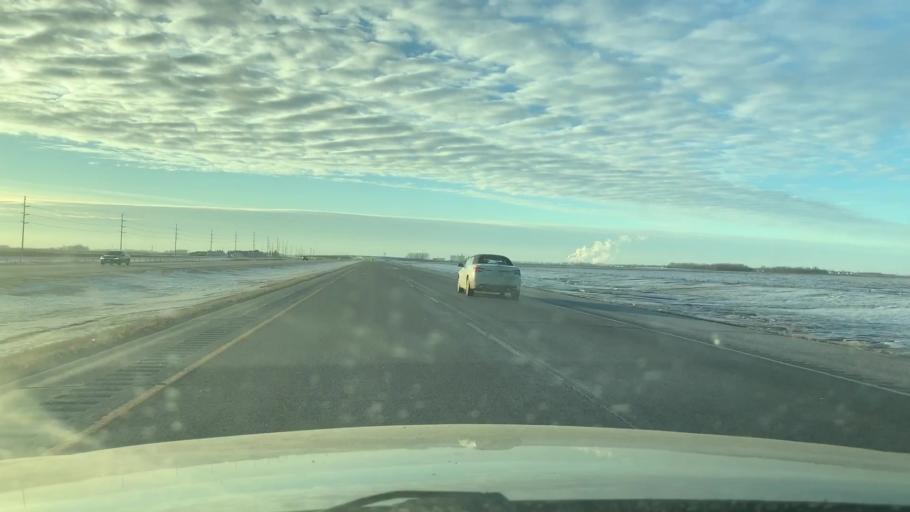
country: US
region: North Dakota
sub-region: Cass County
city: Casselton
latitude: 46.8768
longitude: -97.1381
